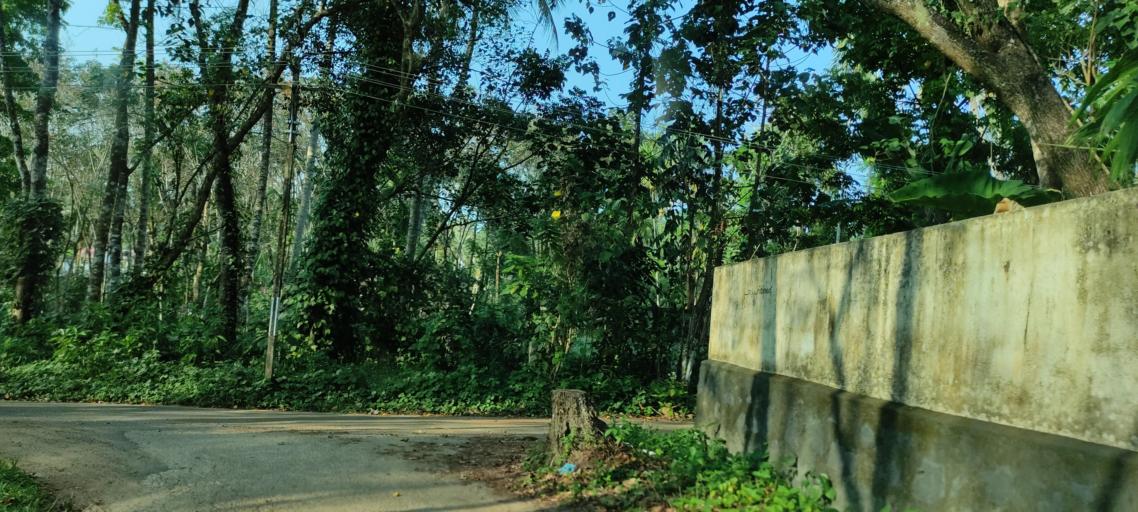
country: IN
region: Kerala
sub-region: Pattanamtitta
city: Adur
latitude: 9.1513
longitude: 76.7584
